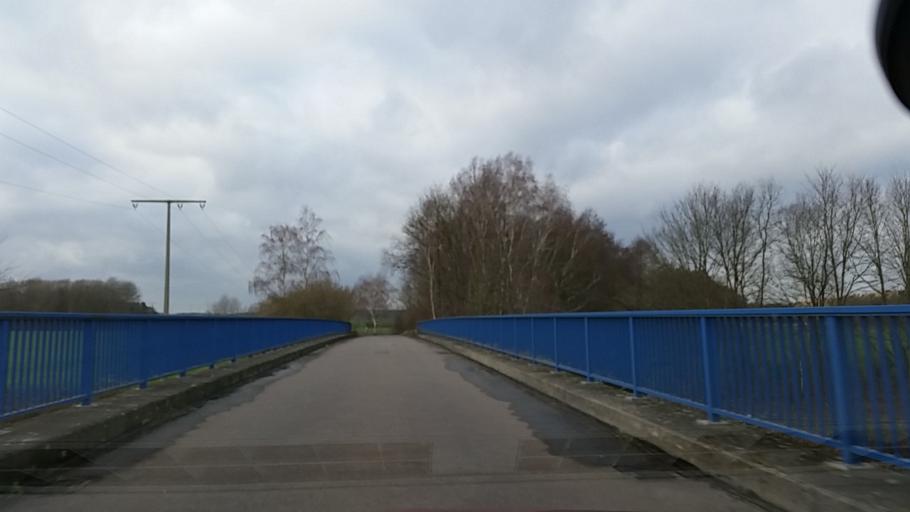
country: DE
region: Lower Saxony
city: Luder
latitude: 52.7640
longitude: 10.6713
